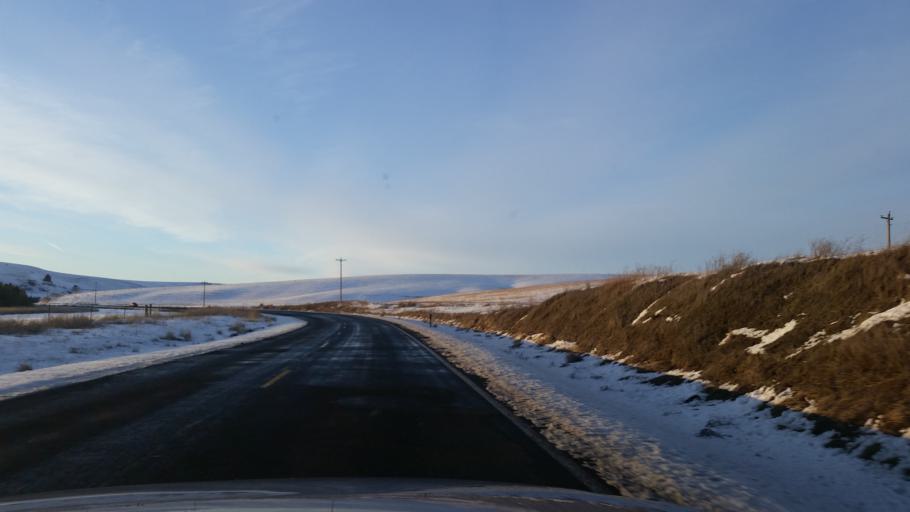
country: US
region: Washington
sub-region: Whitman County
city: Colfax
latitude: 47.1057
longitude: -117.6230
